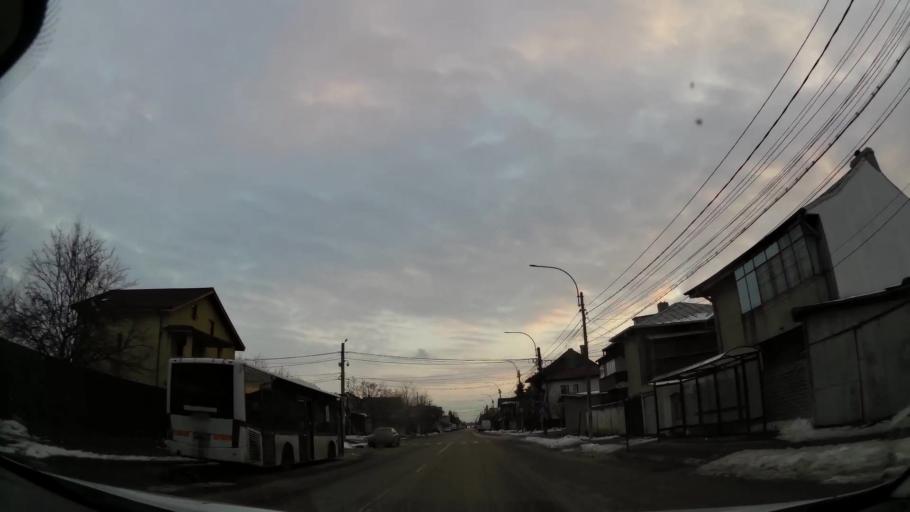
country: RO
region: Ilfov
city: Dobroesti
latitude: 44.4533
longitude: 26.1854
